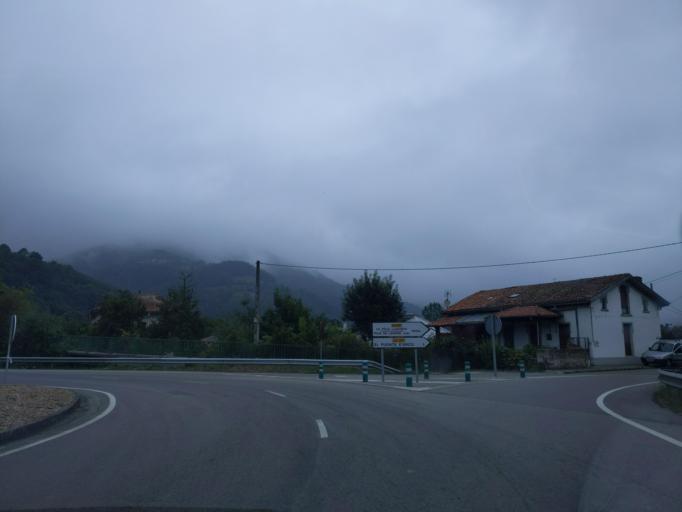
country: ES
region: Asturias
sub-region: Province of Asturias
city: Pola de Laviana
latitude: 43.2356
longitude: -5.5559
